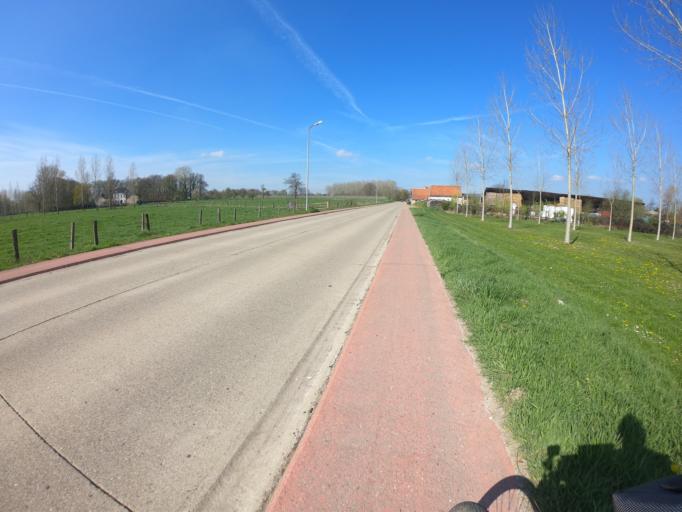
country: BE
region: Flanders
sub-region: Provincie Vlaams-Brabant
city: Geetbets
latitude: 50.9004
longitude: 5.1270
